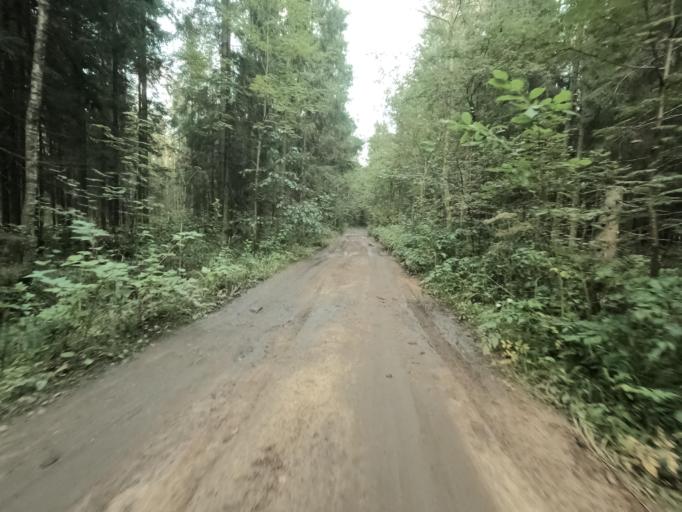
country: RU
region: Leningrad
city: Otradnoye
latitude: 59.8325
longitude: 30.7673
